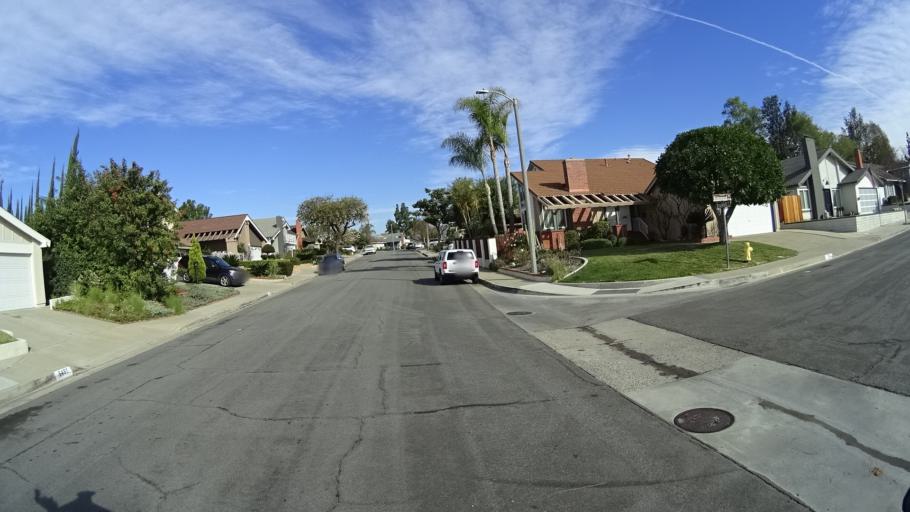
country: US
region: California
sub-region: Orange County
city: Yorba Linda
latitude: 33.8814
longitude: -117.7915
